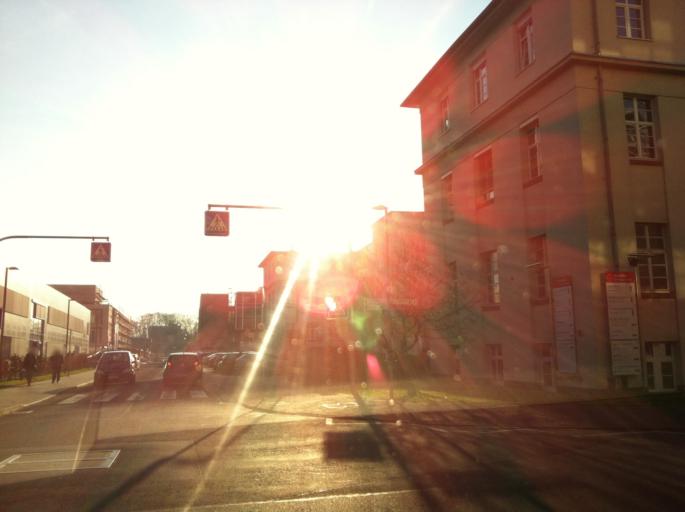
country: DE
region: Hesse
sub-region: Regierungsbezirk Darmstadt
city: Frankfurt am Main
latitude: 50.0949
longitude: 8.6597
